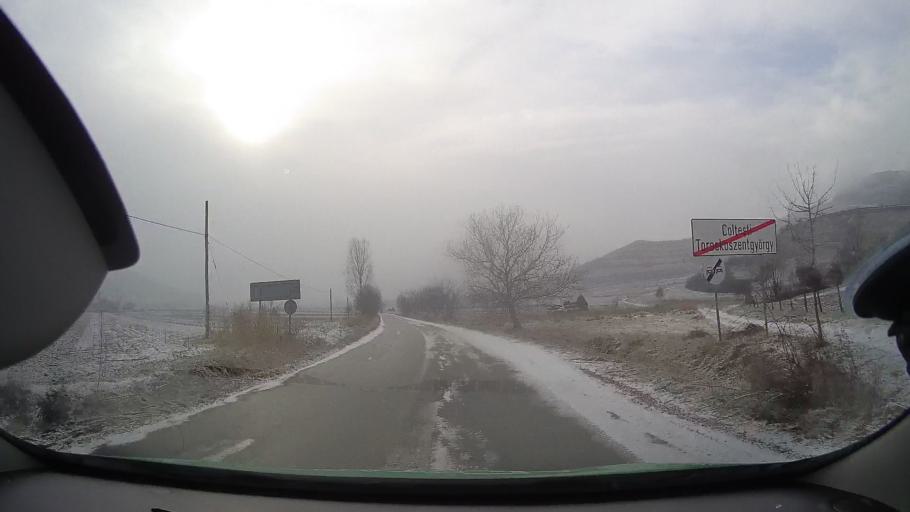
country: RO
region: Alba
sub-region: Comuna Rimetea
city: Rimetea
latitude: 46.4167
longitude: 23.5582
